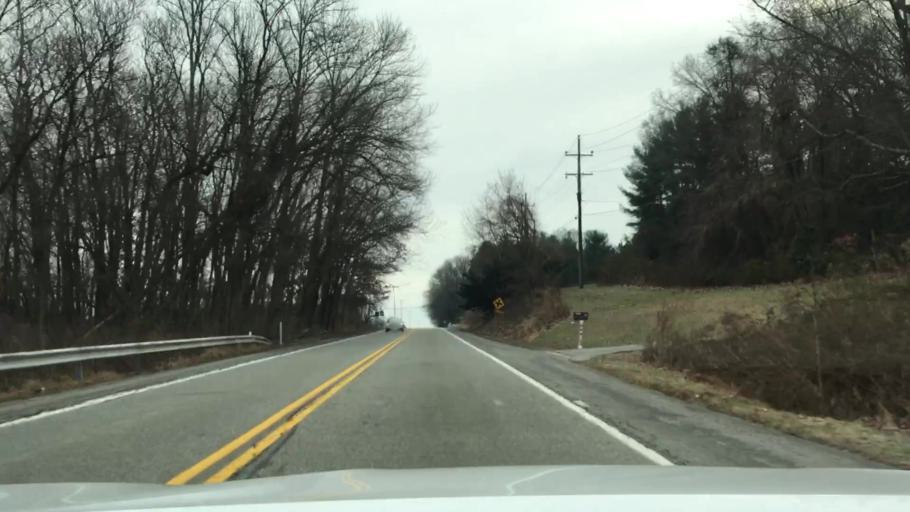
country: US
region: Pennsylvania
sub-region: Chester County
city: Kenilworth
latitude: 40.2219
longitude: -75.6143
